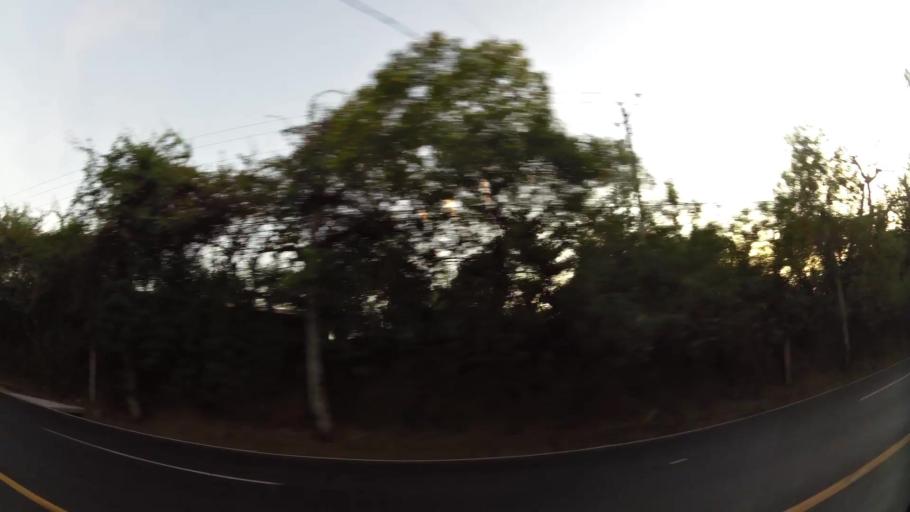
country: SV
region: San Miguel
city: San Miguel
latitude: 13.5010
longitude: -88.2158
